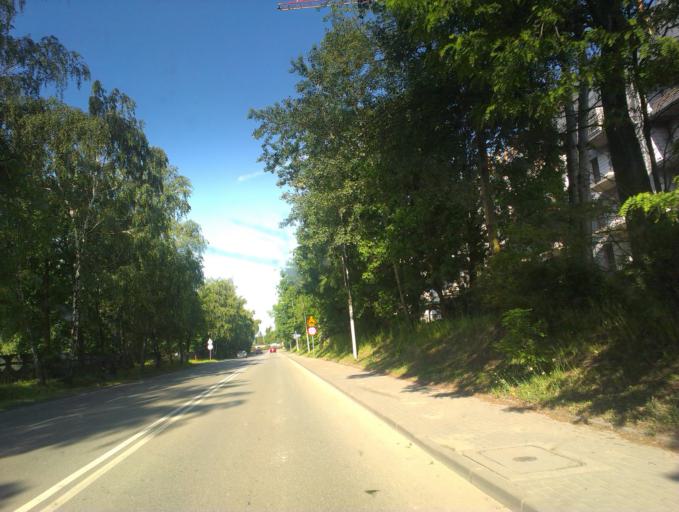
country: PL
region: Silesian Voivodeship
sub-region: Katowice
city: Katowice
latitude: 50.2409
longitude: 19.0290
